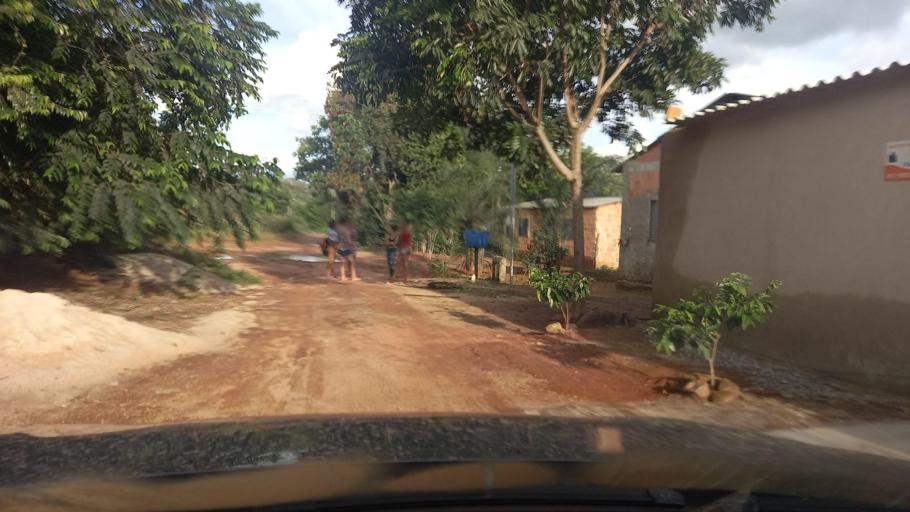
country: BR
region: Goias
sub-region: Cavalcante
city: Cavalcante
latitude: -13.8018
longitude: -47.4447
